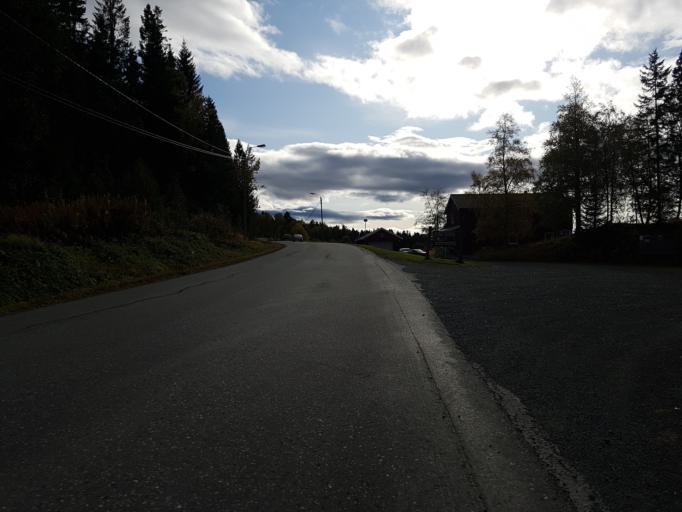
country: NO
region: Sor-Trondelag
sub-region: Klaebu
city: Klaebu
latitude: 63.3956
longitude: 10.5550
